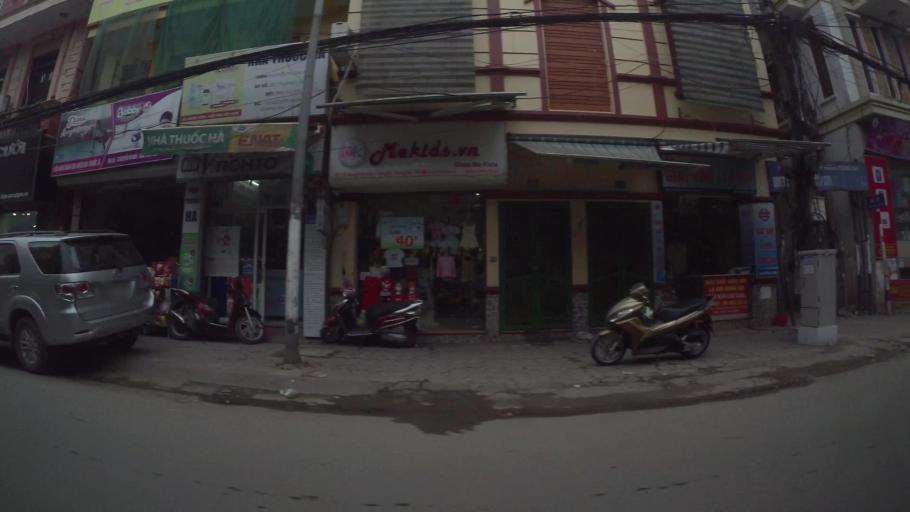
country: VN
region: Ha Noi
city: Hai BaTrung
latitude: 20.9918
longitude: 105.8442
